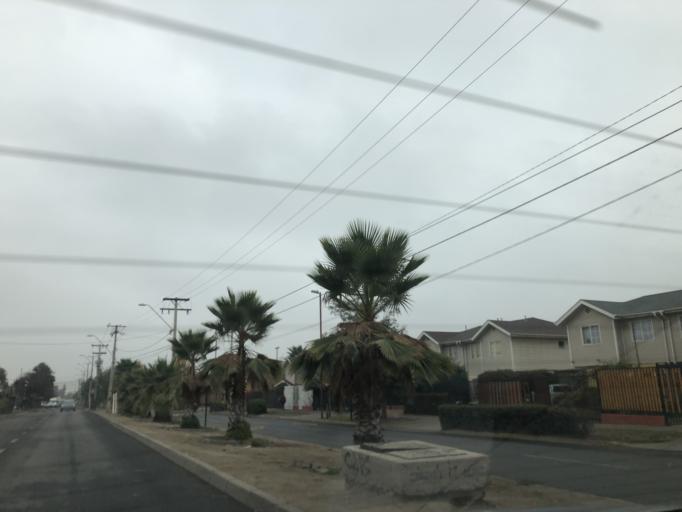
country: CL
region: Santiago Metropolitan
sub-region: Provincia de Cordillera
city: Puente Alto
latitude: -33.5987
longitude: -70.5812
